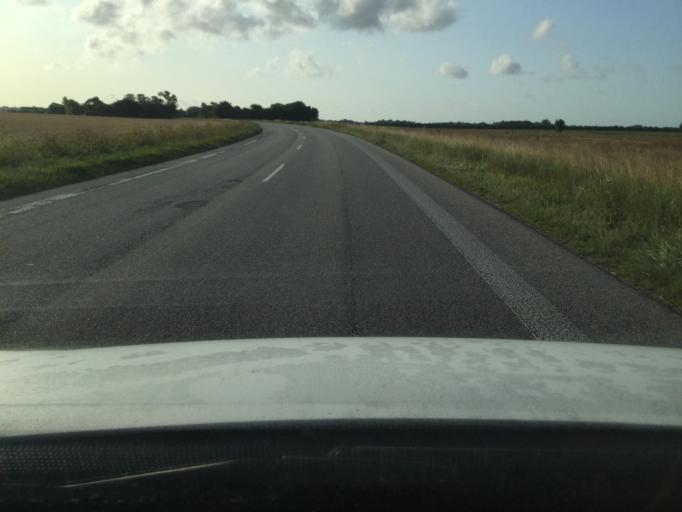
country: DK
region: Zealand
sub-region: Lolland Kommune
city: Rodby
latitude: 54.7673
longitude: 11.3024
